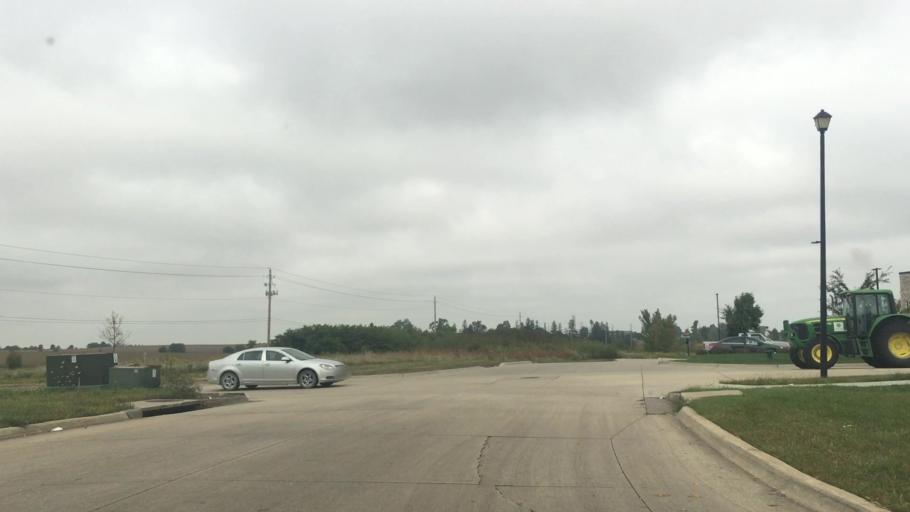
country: US
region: Iowa
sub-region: Linn County
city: Ely
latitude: 41.8920
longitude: -91.6750
